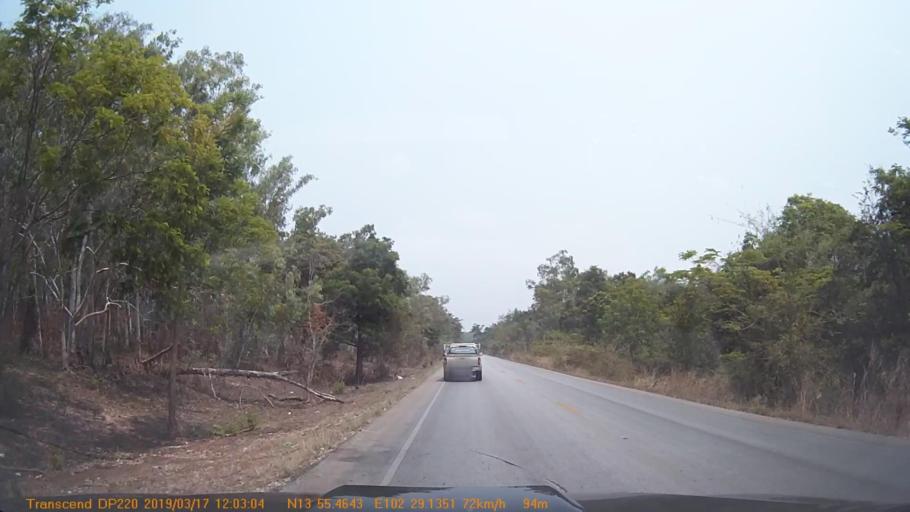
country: TH
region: Sa Kaeo
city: Khok Sung
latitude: 13.9246
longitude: 102.4857
